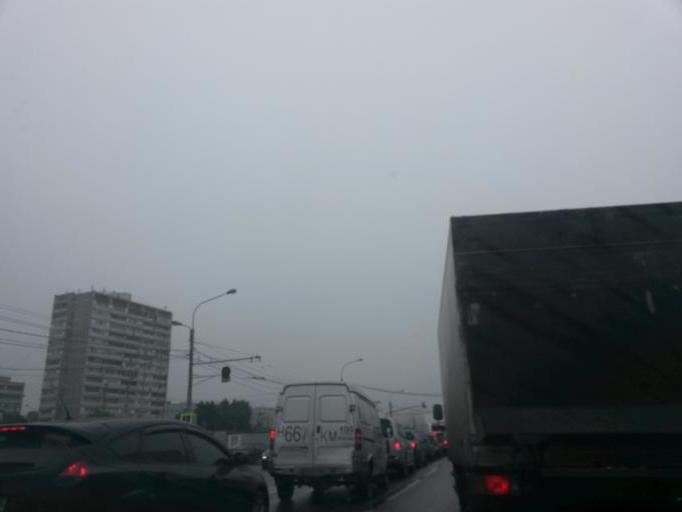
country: RU
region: Moscow
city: Yasenevo
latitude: 55.6335
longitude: 37.5201
